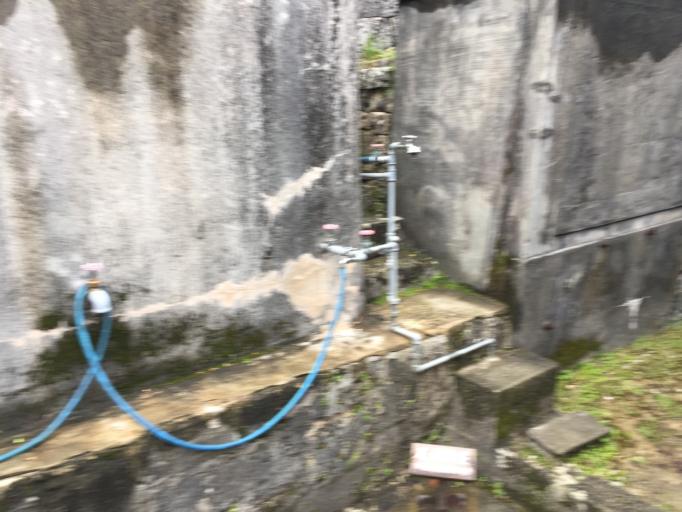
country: JP
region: Okinawa
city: Chatan
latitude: 26.2899
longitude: 127.8006
